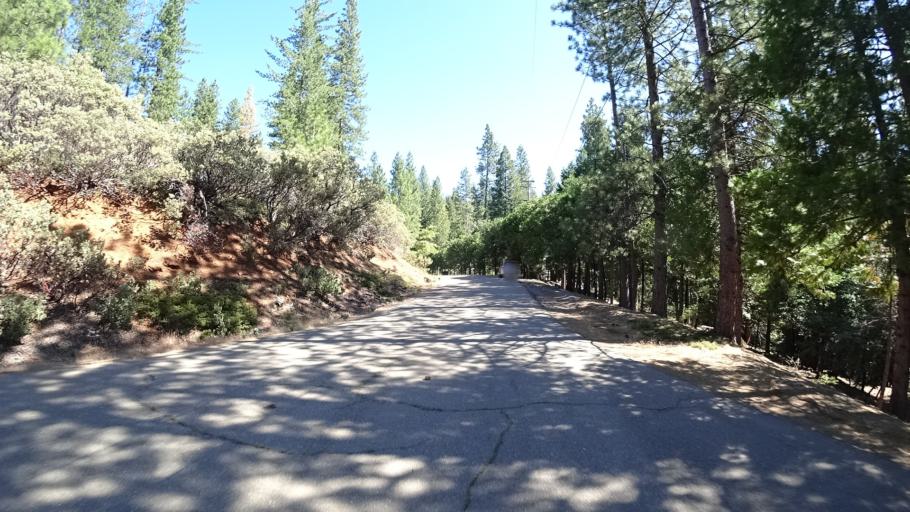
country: US
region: California
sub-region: Calaveras County
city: Arnold
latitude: 38.2403
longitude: -120.3305
